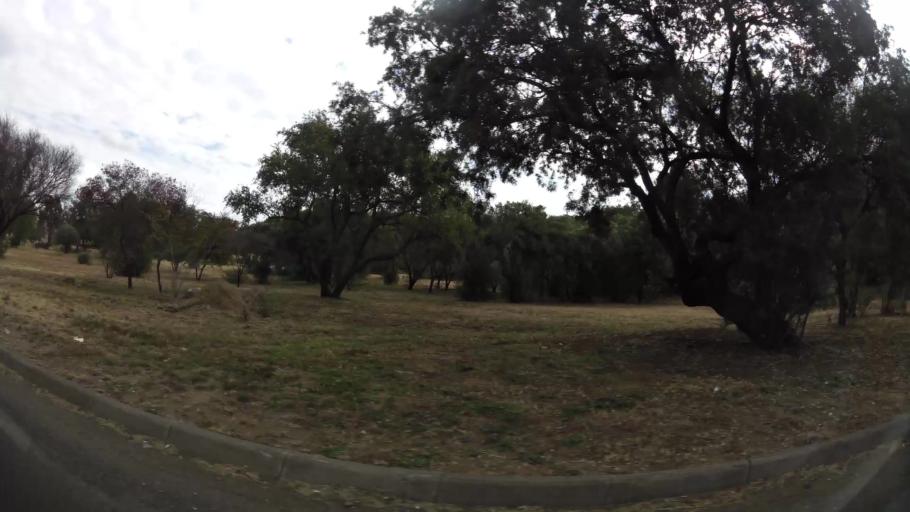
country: ZA
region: Orange Free State
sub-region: Mangaung Metropolitan Municipality
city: Bloemfontein
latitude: -29.1015
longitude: 26.2166
